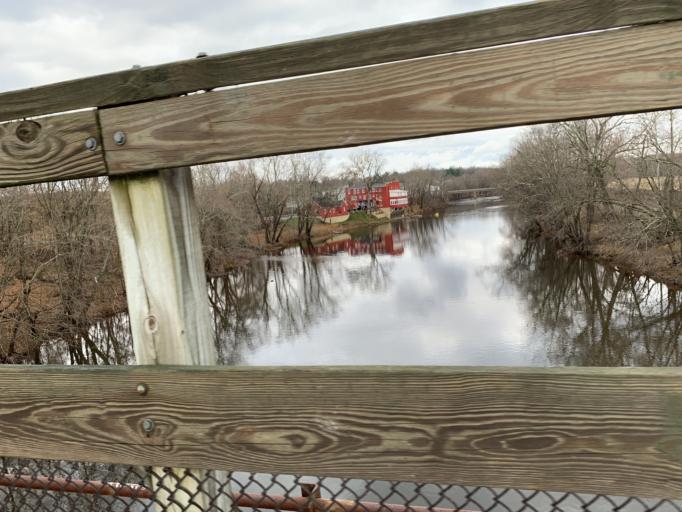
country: US
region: Pennsylvania
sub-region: Montgomery County
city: Trappe
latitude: 40.2211
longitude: -75.4514
